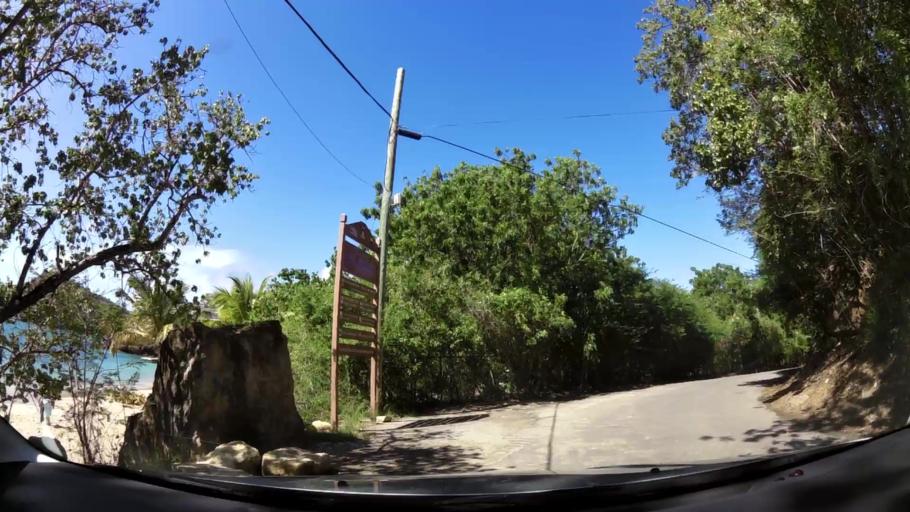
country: AG
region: Saint Paul
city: Falmouth
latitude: 17.0059
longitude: -61.7599
